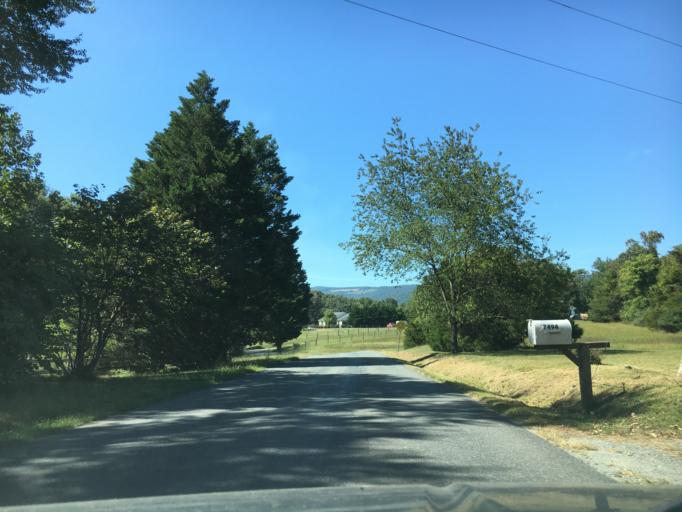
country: US
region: Virginia
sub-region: Albemarle County
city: Crozet
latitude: 38.0168
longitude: -78.7575
